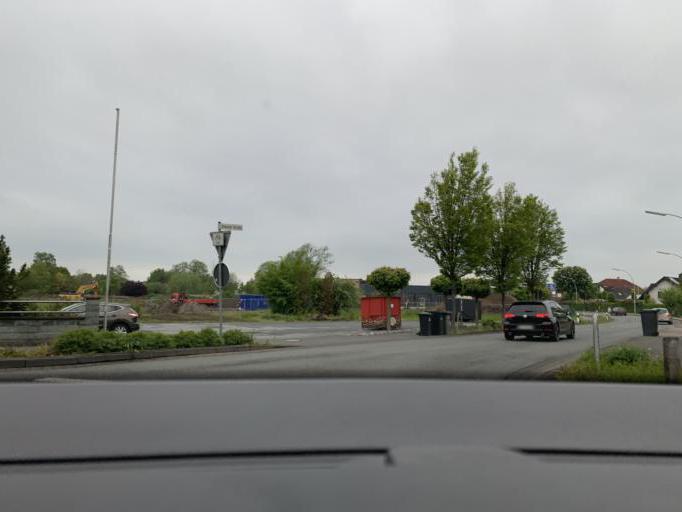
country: DE
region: North Rhine-Westphalia
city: Rietberg
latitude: 51.8043
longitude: 8.4223
